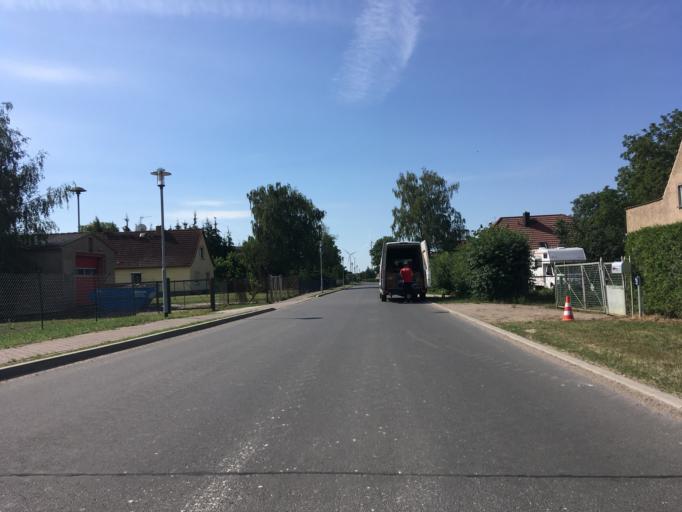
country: DE
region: Brandenburg
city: Gramzow
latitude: 53.2966
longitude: 14.0412
